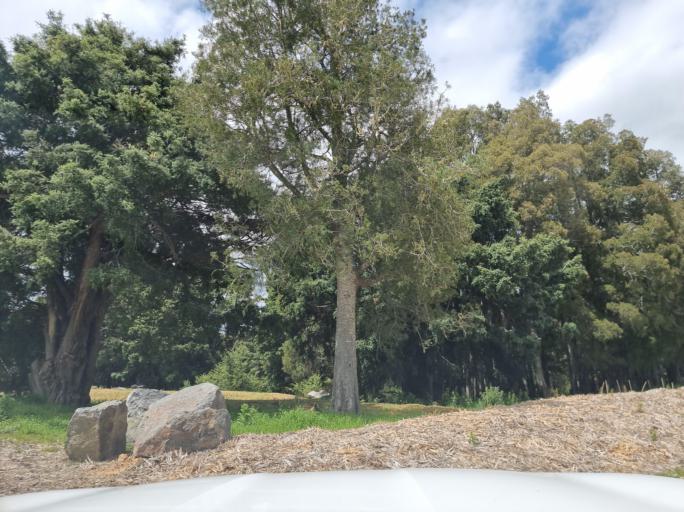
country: NZ
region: Northland
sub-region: Whangarei
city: Ruakaka
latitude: -36.0765
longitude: 174.5492
